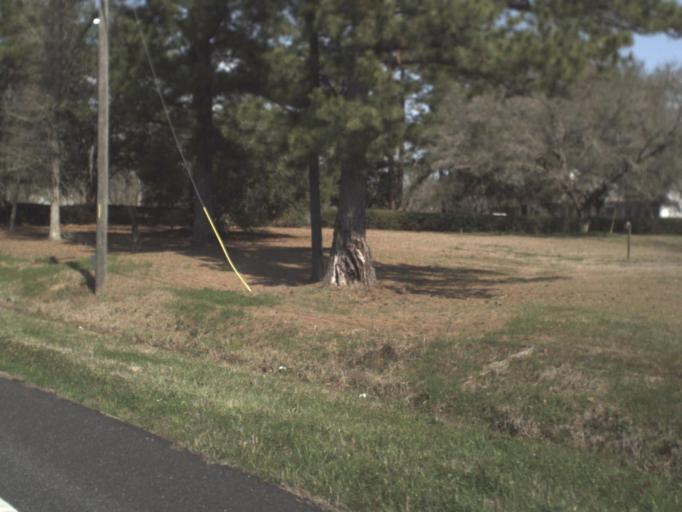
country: US
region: Florida
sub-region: Gadsden County
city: Havana
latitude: 30.5914
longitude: -84.4072
